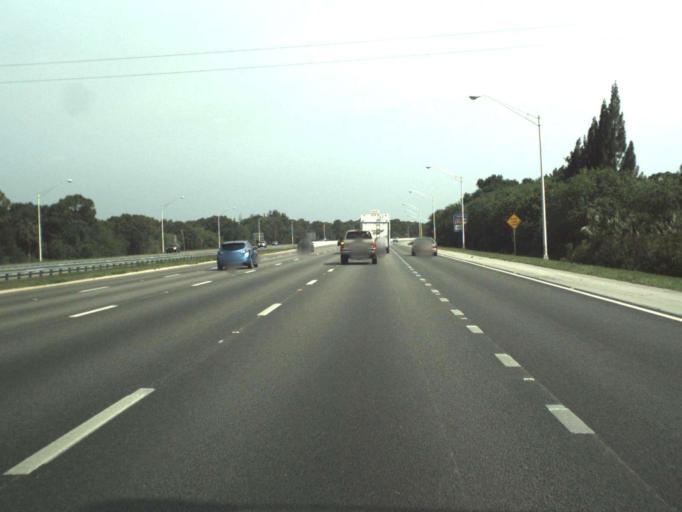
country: US
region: Florida
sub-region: Saint Lucie County
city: Lakewood Park
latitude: 27.4394
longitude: -80.3907
